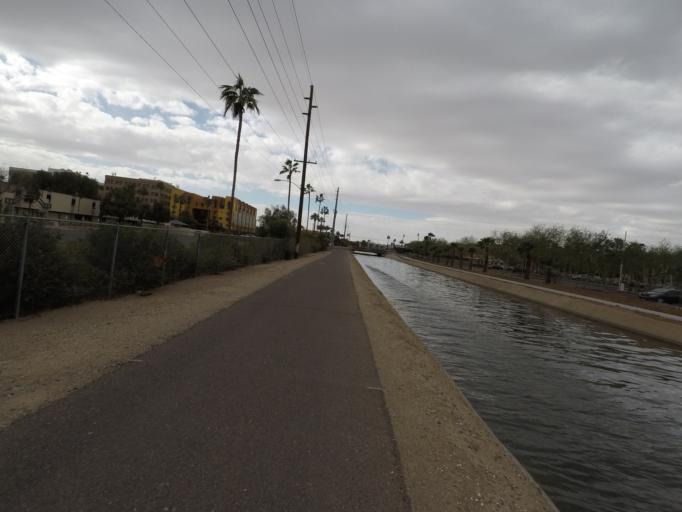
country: US
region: Arizona
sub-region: Maricopa County
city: Phoenix
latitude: 33.5037
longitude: -112.0720
